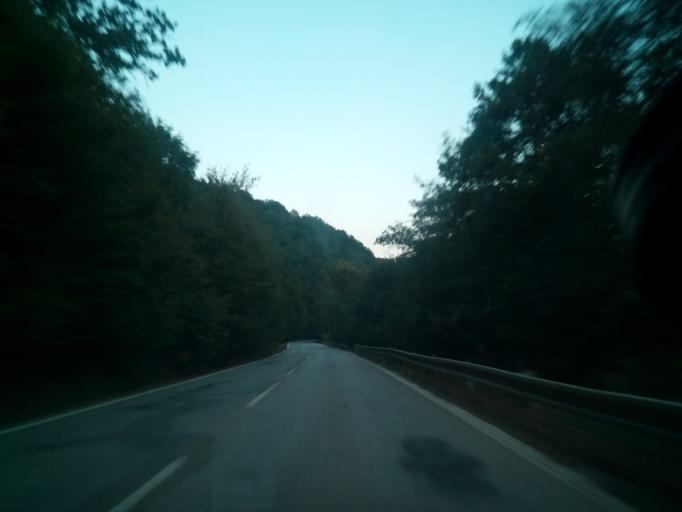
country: SK
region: Kosicky
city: Dobsina
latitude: 48.7978
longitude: 20.3899
